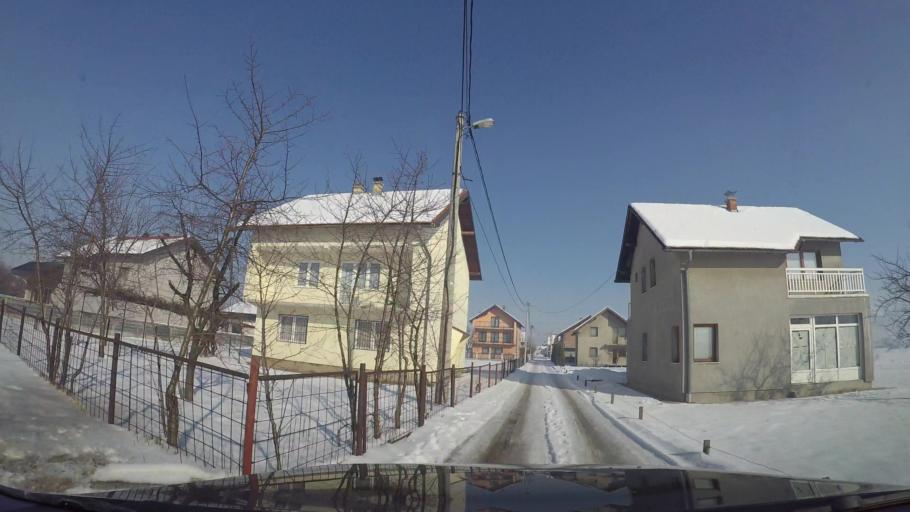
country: BA
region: Federation of Bosnia and Herzegovina
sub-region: Kanton Sarajevo
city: Sarajevo
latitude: 43.8063
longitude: 18.3013
